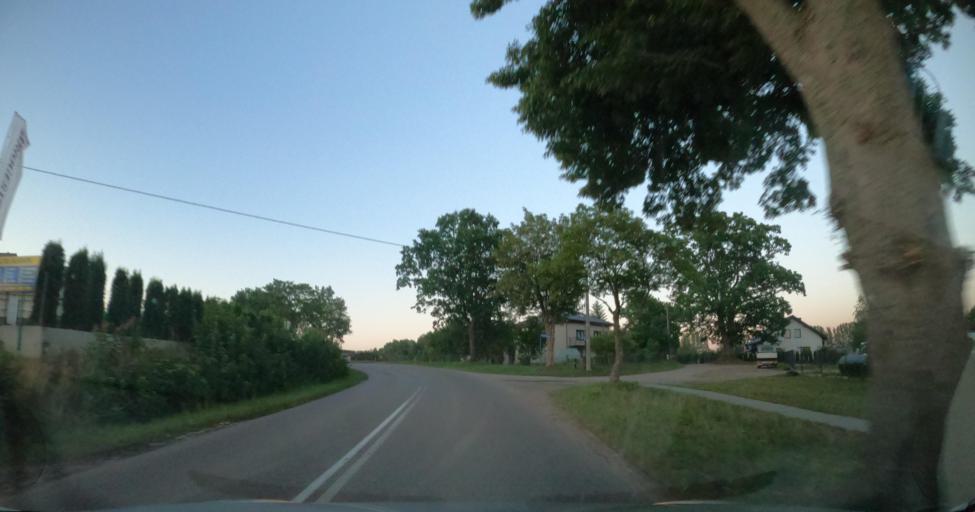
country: PL
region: Pomeranian Voivodeship
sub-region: Powiat wejherowski
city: Linia
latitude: 54.4557
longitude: 18.0352
